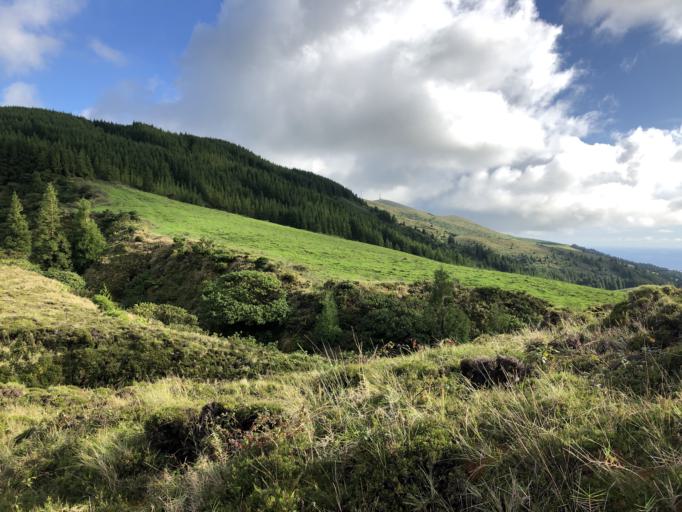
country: PT
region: Azores
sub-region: Ponta Delgada
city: Arrifes
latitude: 37.8337
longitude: -25.7650
